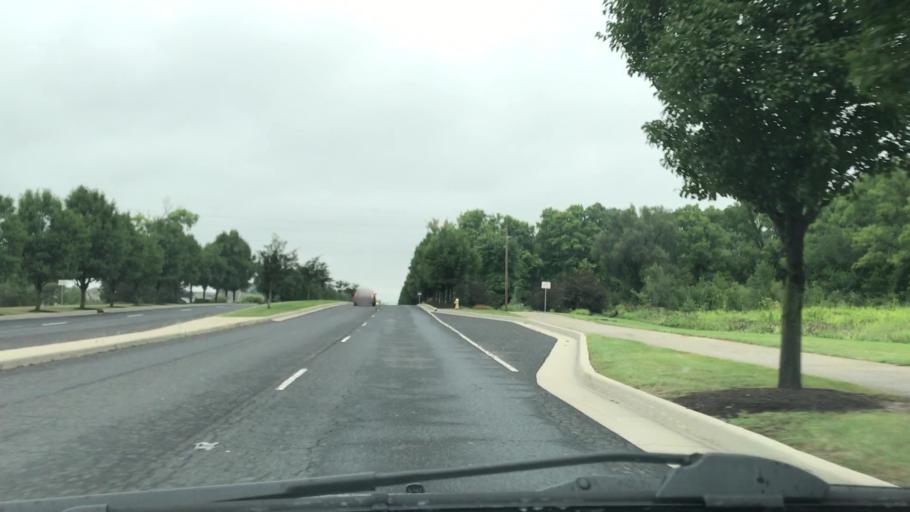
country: US
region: Indiana
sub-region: Hamilton County
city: Carmel
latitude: 40.0063
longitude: -86.0705
